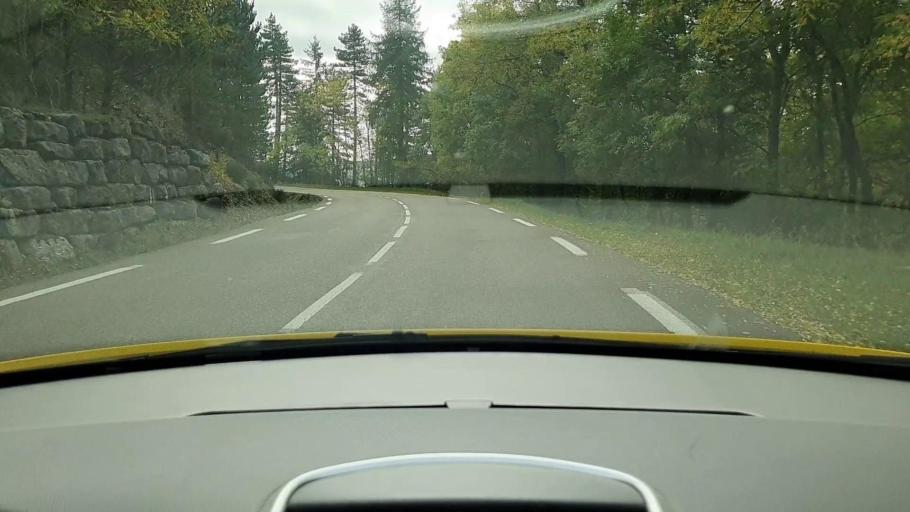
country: FR
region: Languedoc-Roussillon
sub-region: Departement de la Lozere
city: Meyrueis
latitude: 44.1262
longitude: 3.4455
